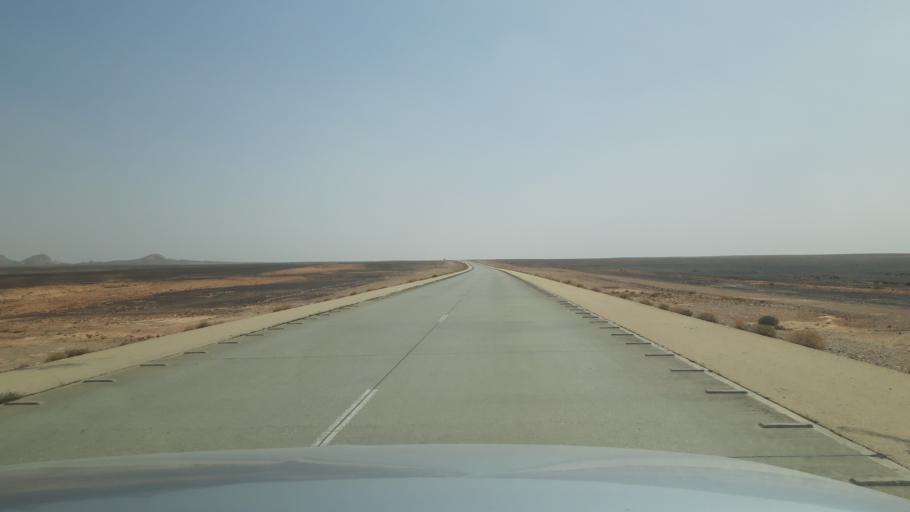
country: SA
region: Al Jawf
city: Al Qurayyat
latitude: 31.0163
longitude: 36.6337
